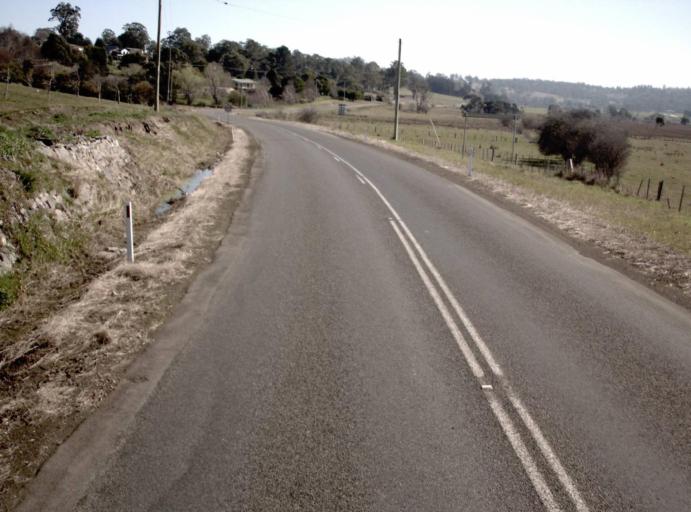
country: AU
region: Tasmania
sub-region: Launceston
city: Mayfield
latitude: -41.3294
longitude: 147.0708
